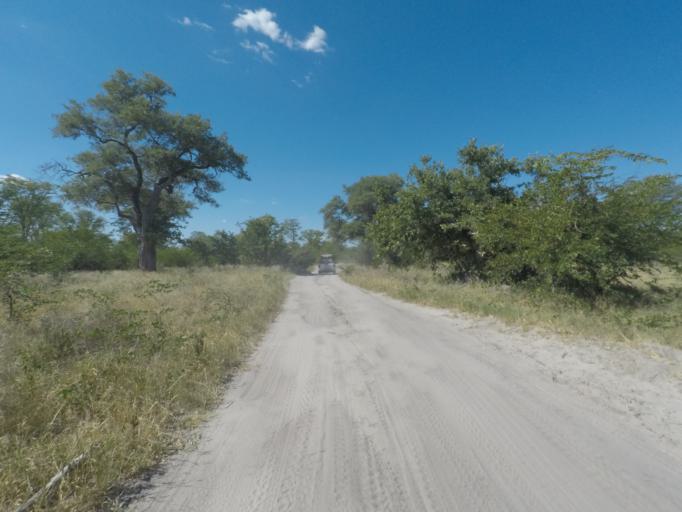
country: BW
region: North West
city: Maun
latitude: -19.4245
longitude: 23.6365
